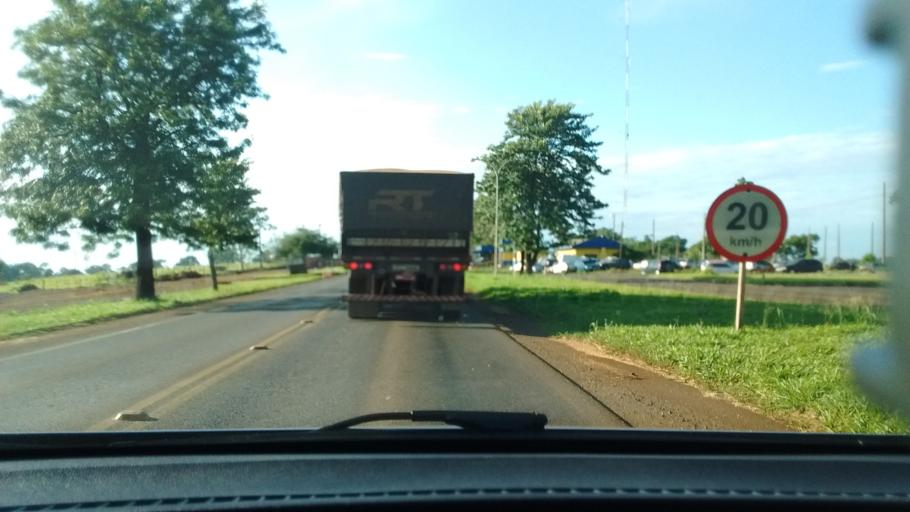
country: BR
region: Parana
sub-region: Cascavel
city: Cascavel
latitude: -25.1820
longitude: -53.6019
